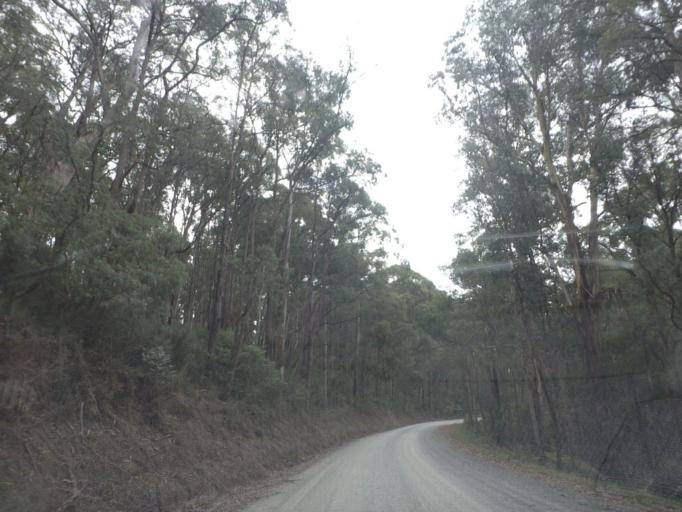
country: AU
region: Victoria
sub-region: Murrindindi
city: Alexandra
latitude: -37.4779
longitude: 145.9777
